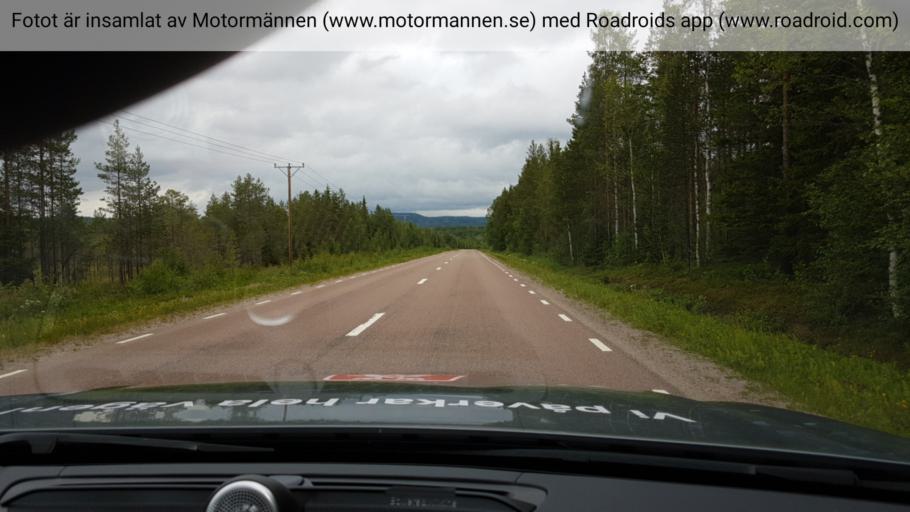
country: SE
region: Jaemtland
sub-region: Braecke Kommun
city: Braecke
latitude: 62.9344
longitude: 15.6940
